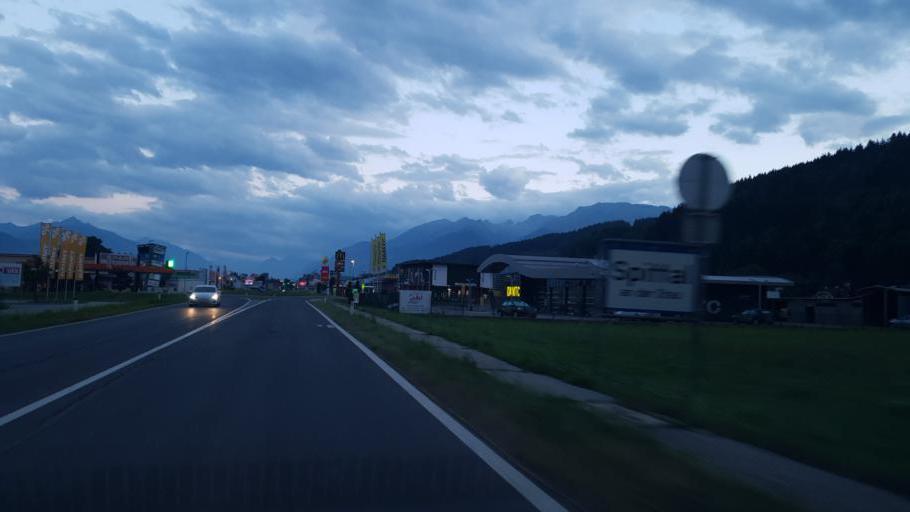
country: AT
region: Carinthia
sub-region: Politischer Bezirk Spittal an der Drau
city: Spittal an der Drau
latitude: 46.7859
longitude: 13.5245
